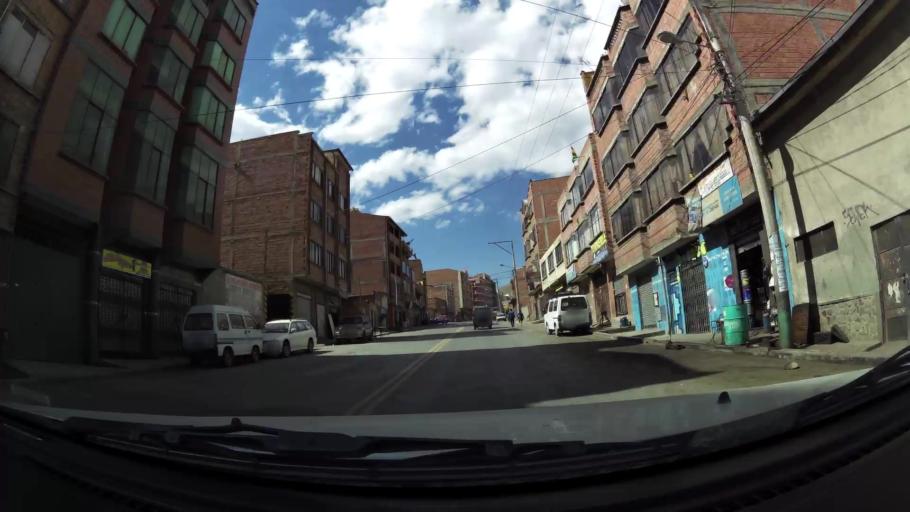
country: BO
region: La Paz
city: La Paz
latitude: -16.4618
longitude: -68.1062
